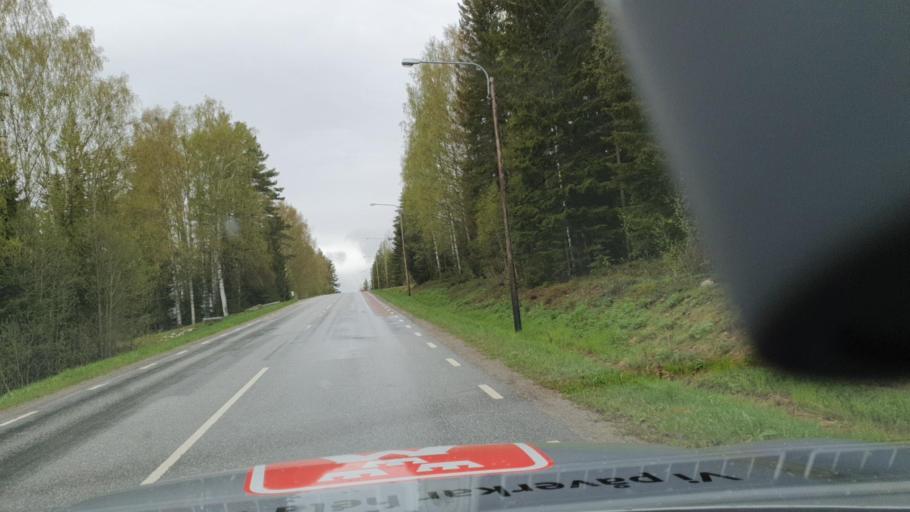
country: SE
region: Vaesternorrland
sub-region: OErnskoeldsviks Kommun
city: Bjasta
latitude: 63.3821
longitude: 18.4725
